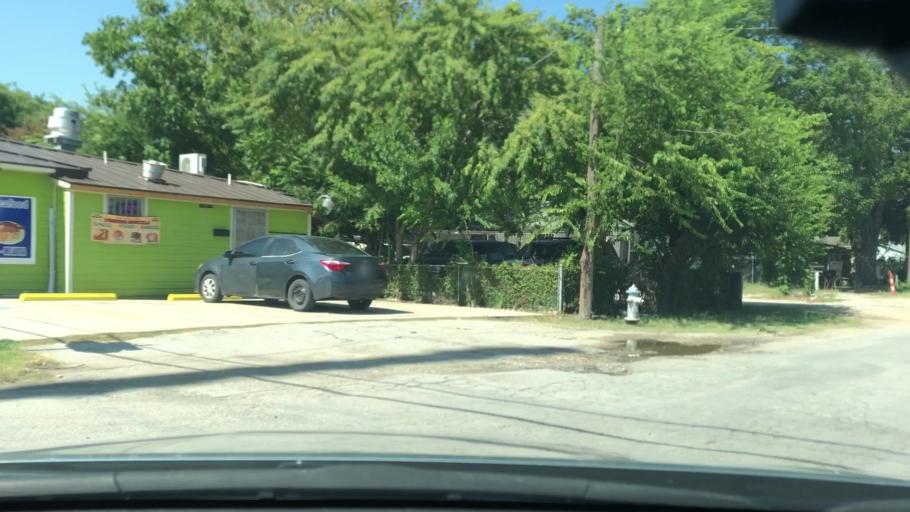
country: US
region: Texas
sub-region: Bexar County
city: Windcrest
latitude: 29.4931
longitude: -98.3928
